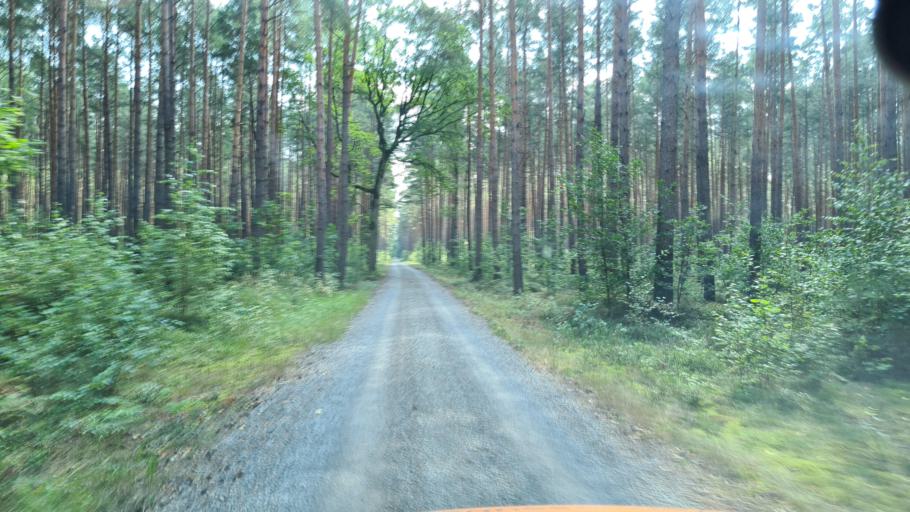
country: DE
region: Brandenburg
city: Hohenbucko
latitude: 51.8052
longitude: 13.5547
